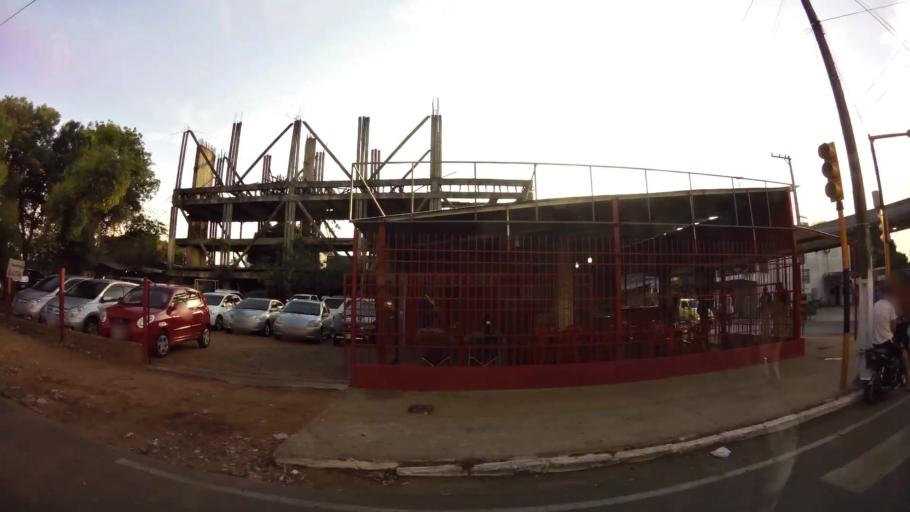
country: PY
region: Central
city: San Lorenzo
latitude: -25.3454
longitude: -57.5048
